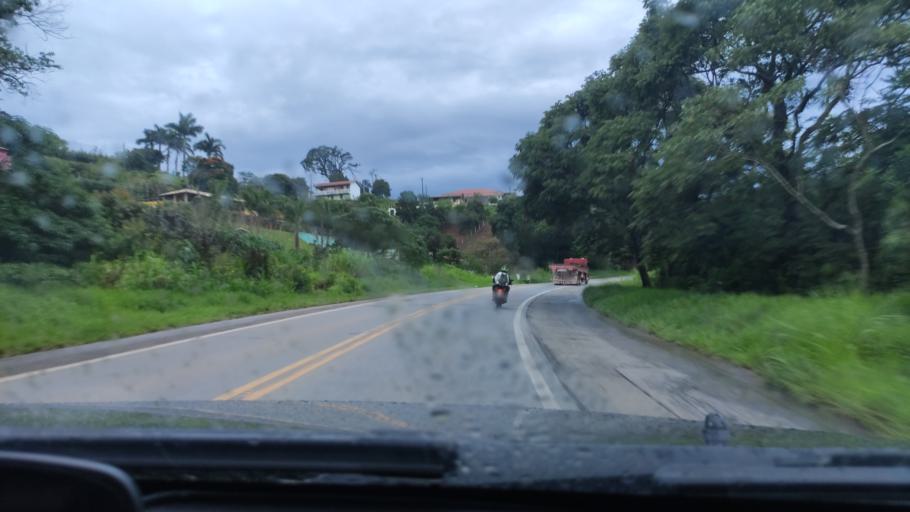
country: BR
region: Sao Paulo
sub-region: Socorro
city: Socorro
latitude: -22.7660
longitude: -46.5587
